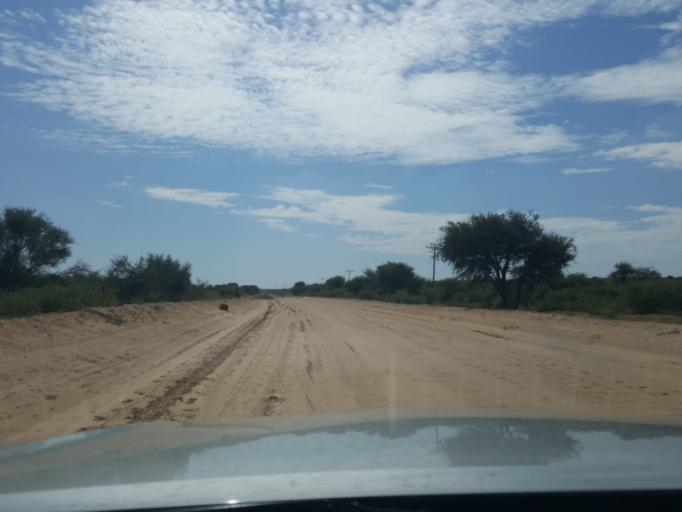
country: BW
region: Kweneng
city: Letlhakeng
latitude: -24.0477
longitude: 25.0205
